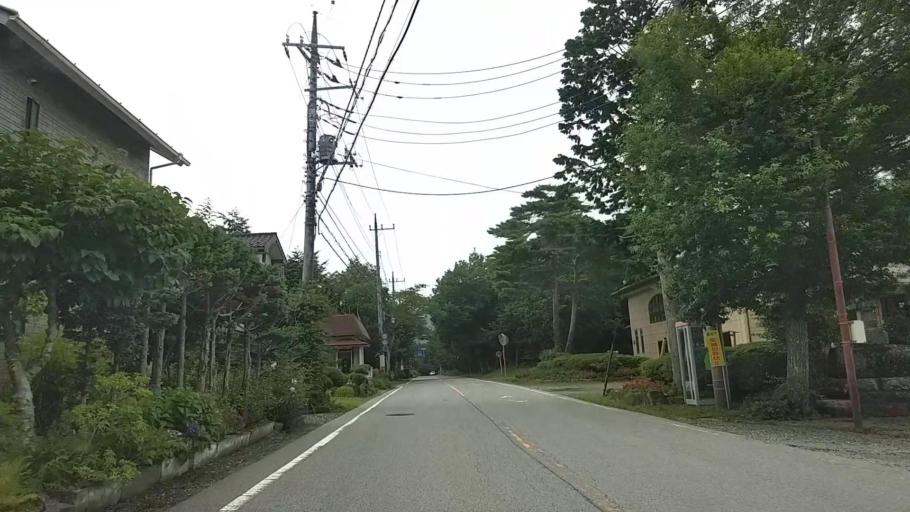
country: JP
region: Yamanashi
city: Fujikawaguchiko
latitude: 35.4924
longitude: 138.6769
